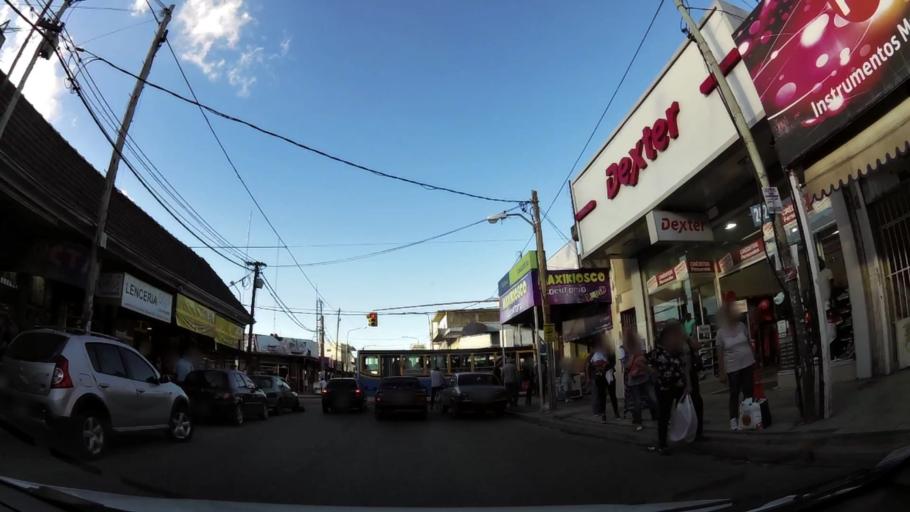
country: AR
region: Buenos Aires
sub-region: Partido de Moron
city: Moron
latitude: -34.6986
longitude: -58.6261
